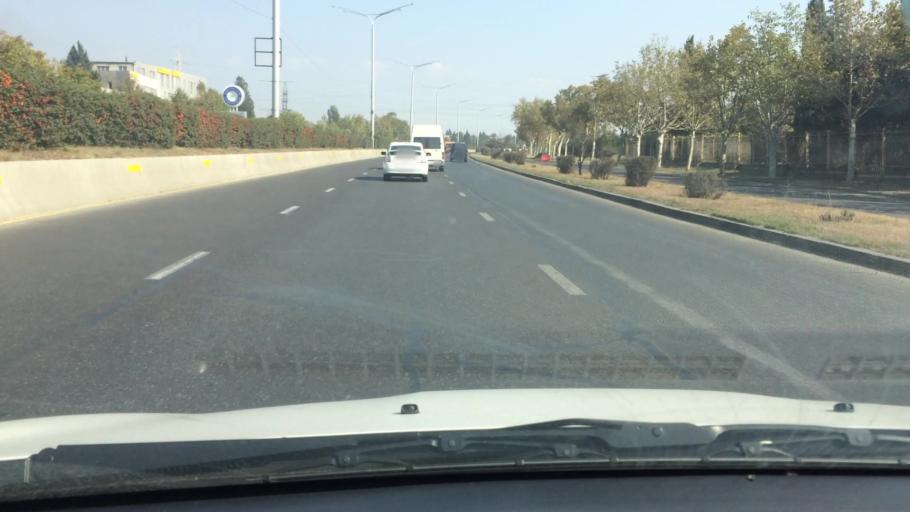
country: GE
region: T'bilisi
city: Tbilisi
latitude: 41.6888
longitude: 44.9060
